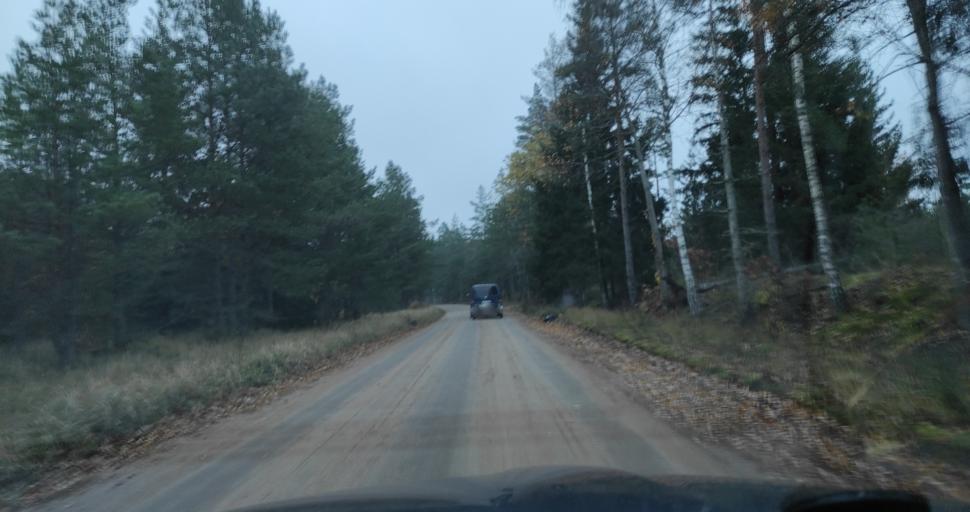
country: LV
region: Pavilostas
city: Pavilosta
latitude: 56.7586
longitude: 21.2709
